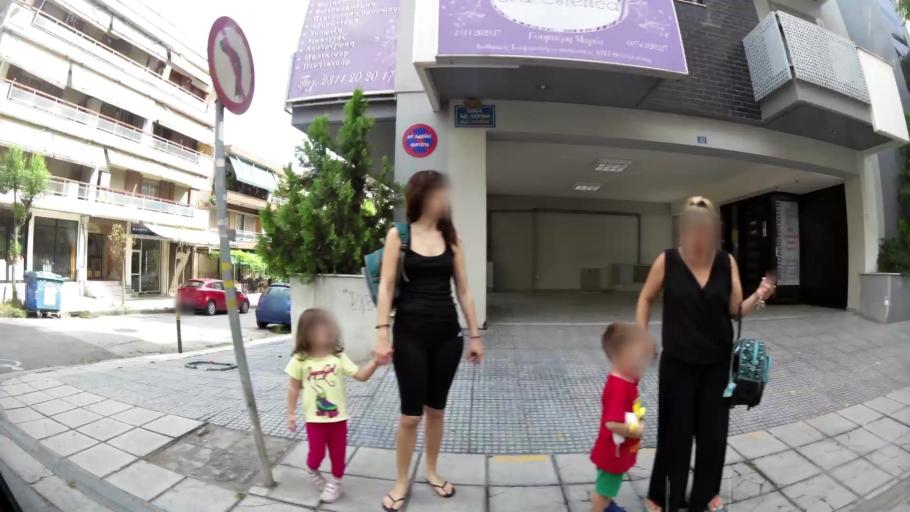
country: GR
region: Central Macedonia
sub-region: Nomos Thessalonikis
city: Kalamaria
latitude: 40.5750
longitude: 22.9515
